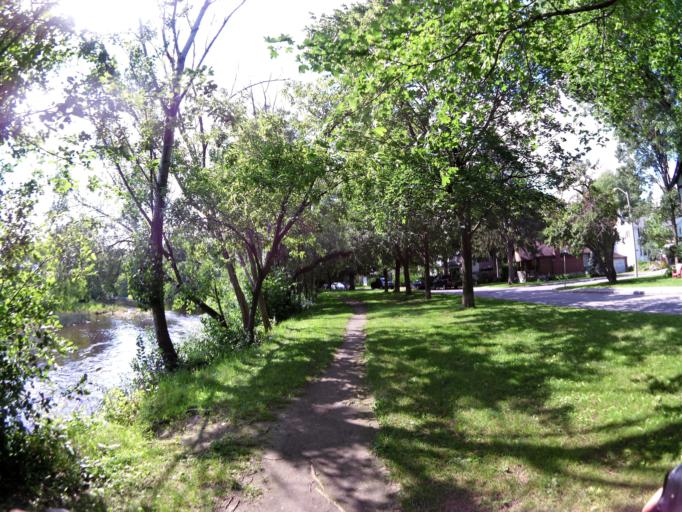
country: CA
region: Ontario
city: Ottawa
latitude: 45.3890
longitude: -75.6806
